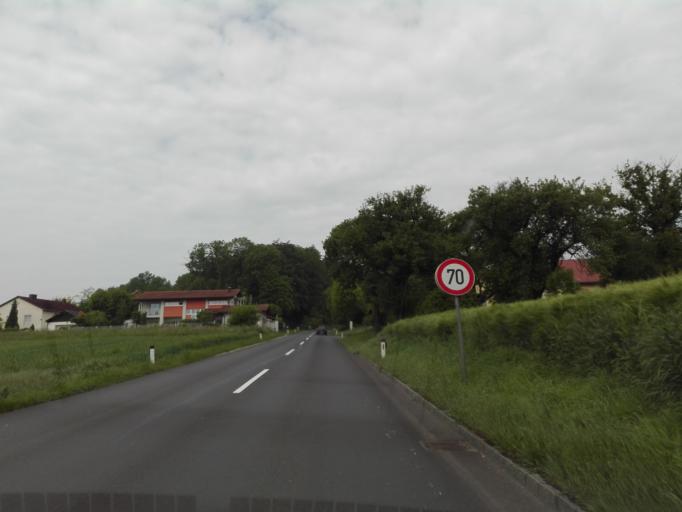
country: AT
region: Upper Austria
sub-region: Politischer Bezirk Linz-Land
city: Pasching
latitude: 48.2722
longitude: 14.1905
